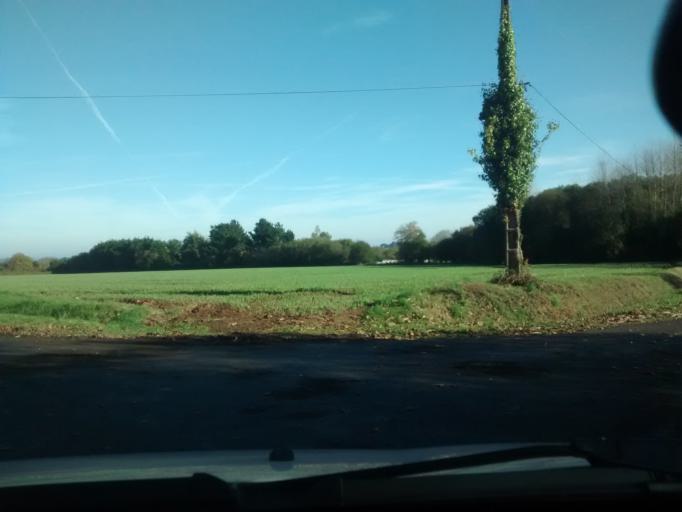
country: FR
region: Brittany
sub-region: Departement des Cotes-d'Armor
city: Saint-Quay-Perros
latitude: 48.7817
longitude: -3.4297
